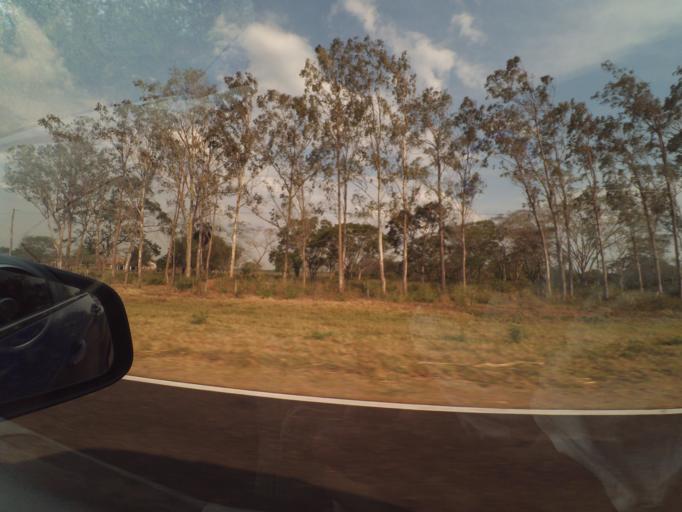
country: BO
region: Santa Cruz
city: Montero
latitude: -17.2693
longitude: -63.0867
